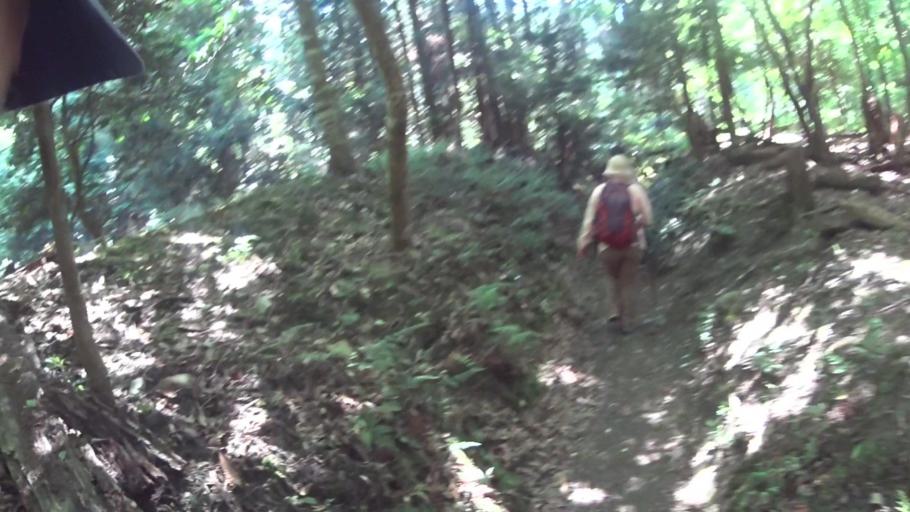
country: JP
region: Kyoto
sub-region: Kyoto-shi
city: Kamigyo-ku
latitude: 35.0181
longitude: 135.8075
